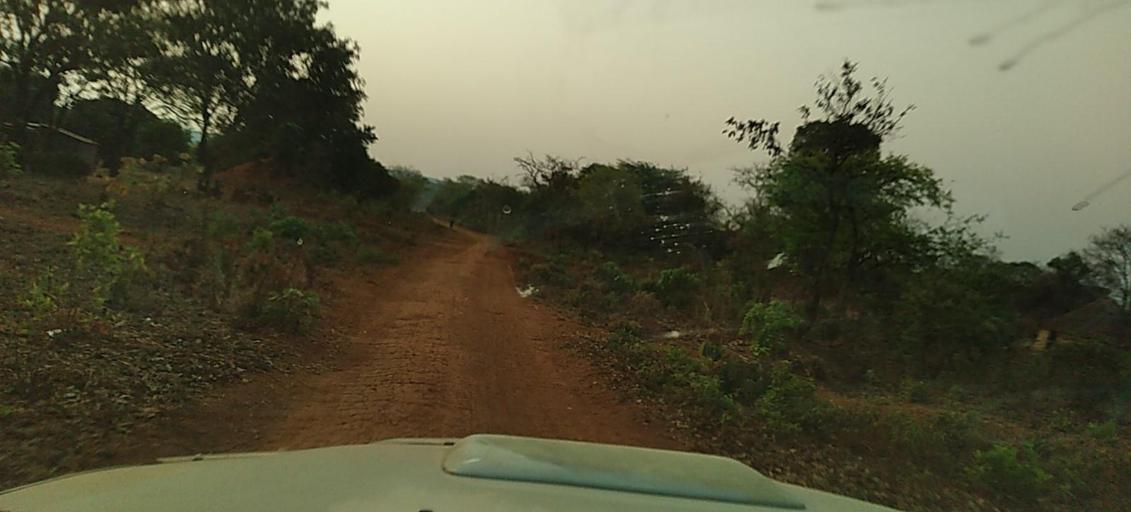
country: ZM
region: North-Western
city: Kasempa
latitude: -13.0740
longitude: 26.3859
